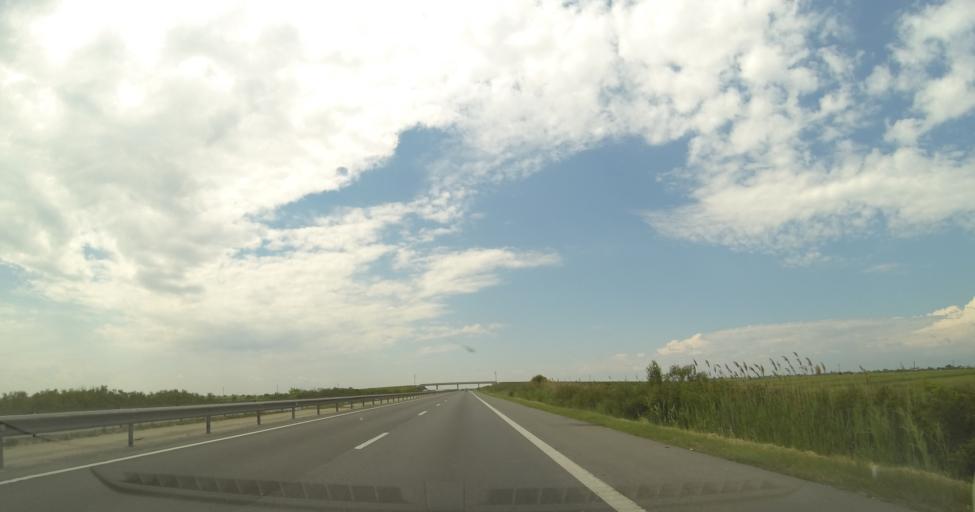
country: RO
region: Dambovita
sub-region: Comuna Petresti
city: Ionesti
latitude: 44.6717
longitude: 25.2970
